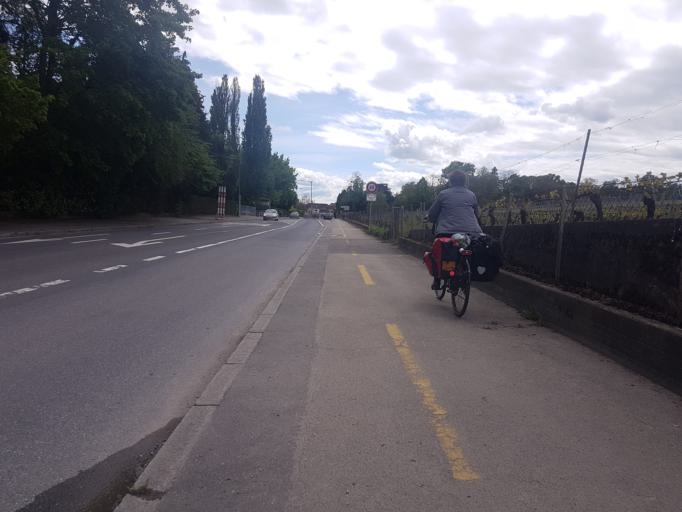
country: CH
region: Vaud
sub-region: Nyon District
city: Coppet
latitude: 46.3209
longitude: 6.1961
